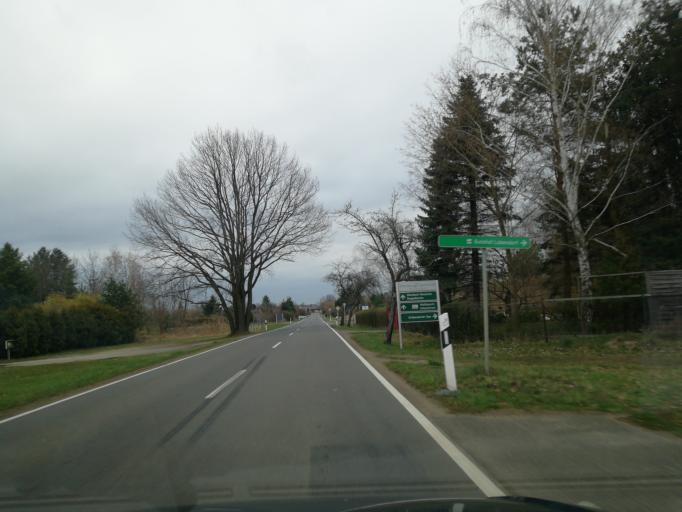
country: DE
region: Brandenburg
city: Vetschau
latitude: 51.7741
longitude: 14.0692
